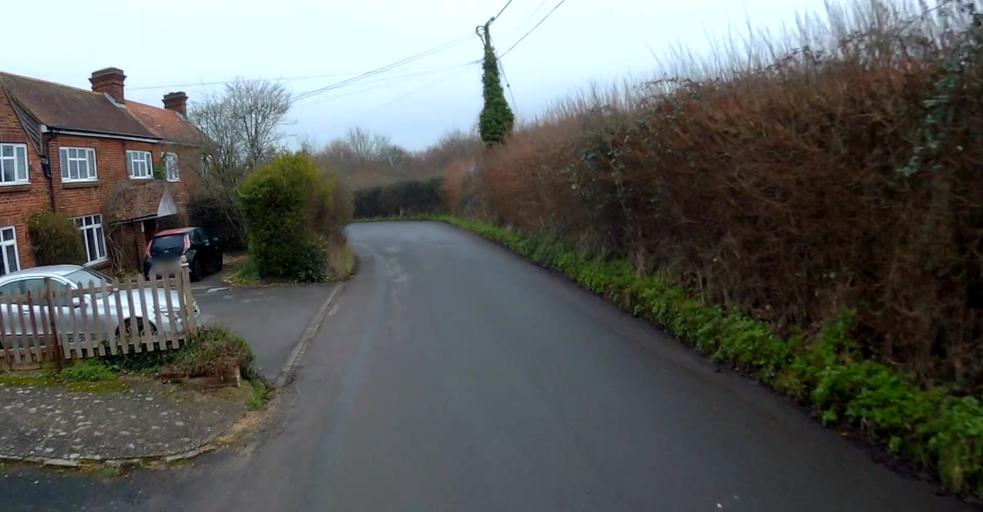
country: GB
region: England
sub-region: Hampshire
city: Old Basing
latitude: 51.2766
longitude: -1.0519
